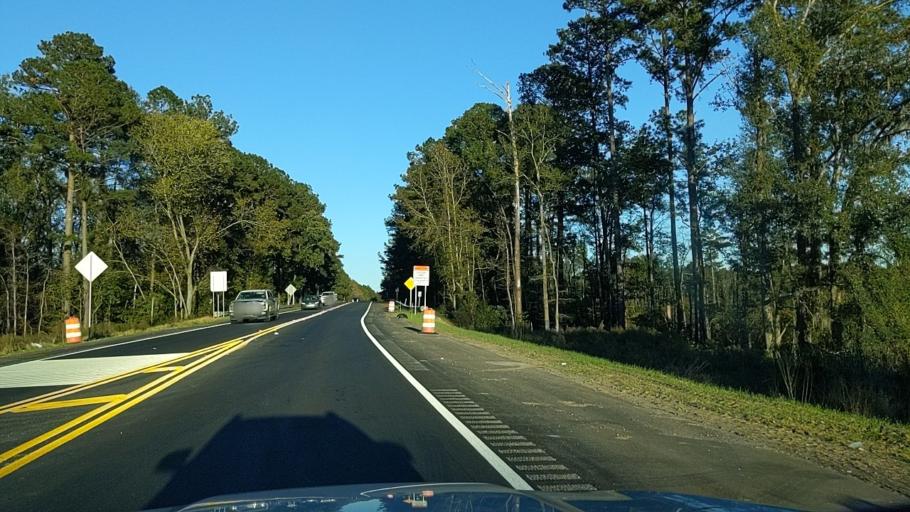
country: US
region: Georgia
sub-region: Chatham County
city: Port Wentworth
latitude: 32.1933
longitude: -81.2216
